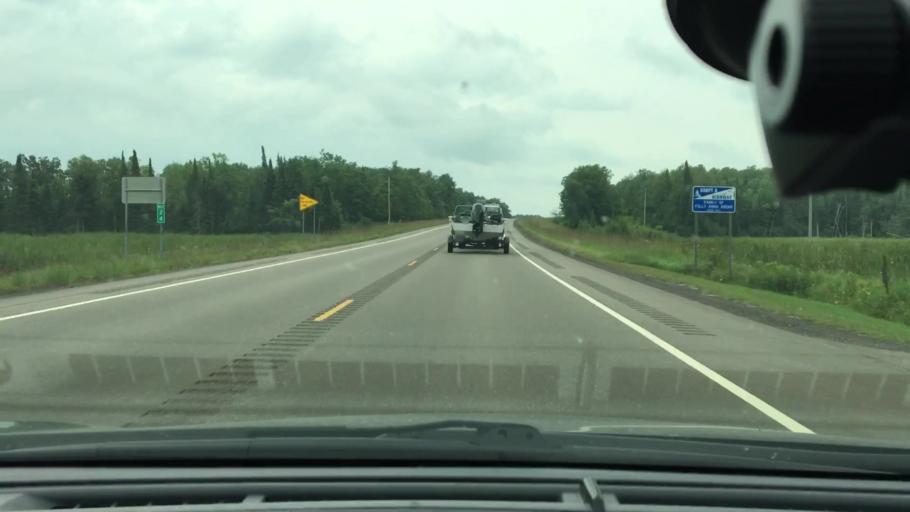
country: US
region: Minnesota
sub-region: Crow Wing County
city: Crosby
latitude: 46.6234
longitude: -93.9465
